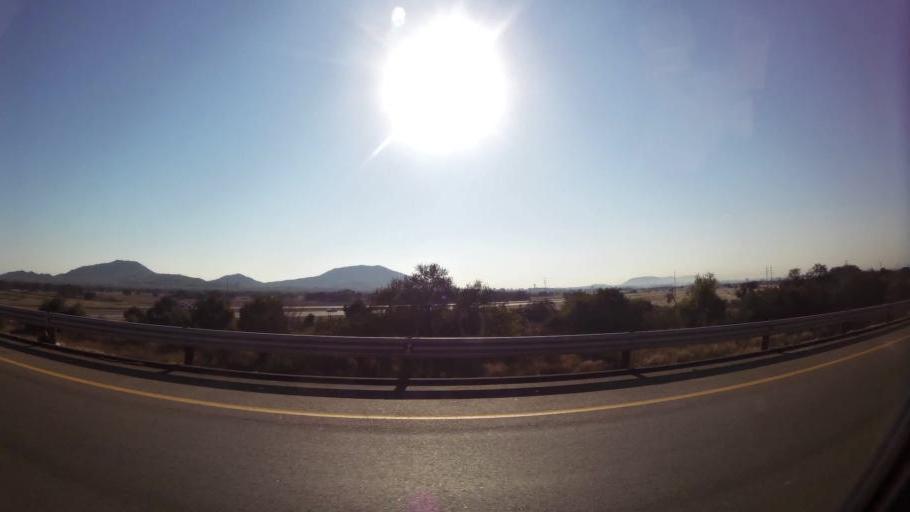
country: ZA
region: Gauteng
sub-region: City of Tshwane Metropolitan Municipality
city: Pretoria
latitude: -25.6478
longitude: 28.1536
